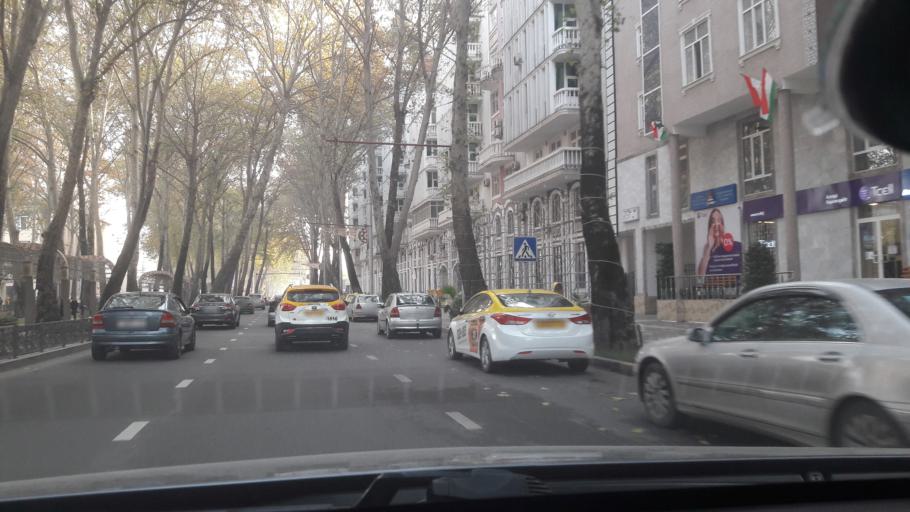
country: TJ
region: Dushanbe
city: Dushanbe
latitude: 38.5729
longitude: 68.7875
